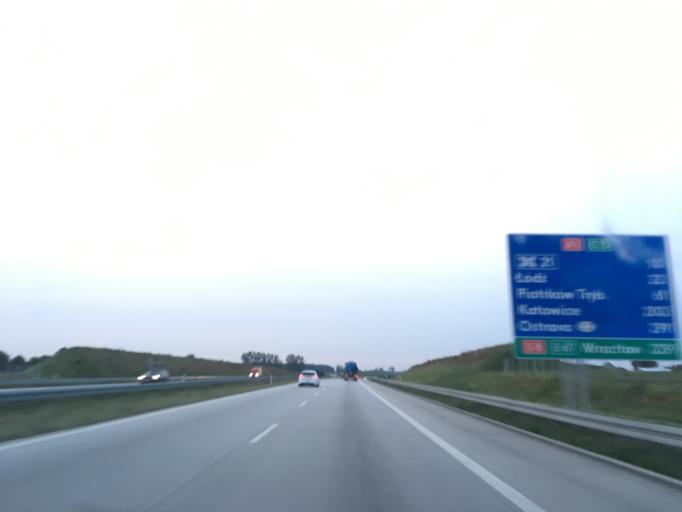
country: PL
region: Lodz Voivodeship
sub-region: Powiat zgierski
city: Strykow
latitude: 51.8734
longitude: 19.6512
